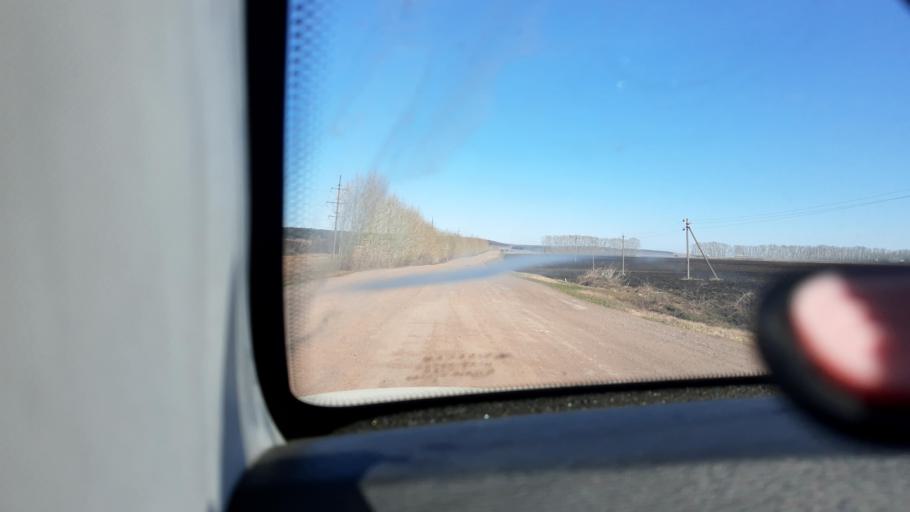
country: RU
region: Bashkortostan
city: Asanovo
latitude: 54.9592
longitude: 55.5699
